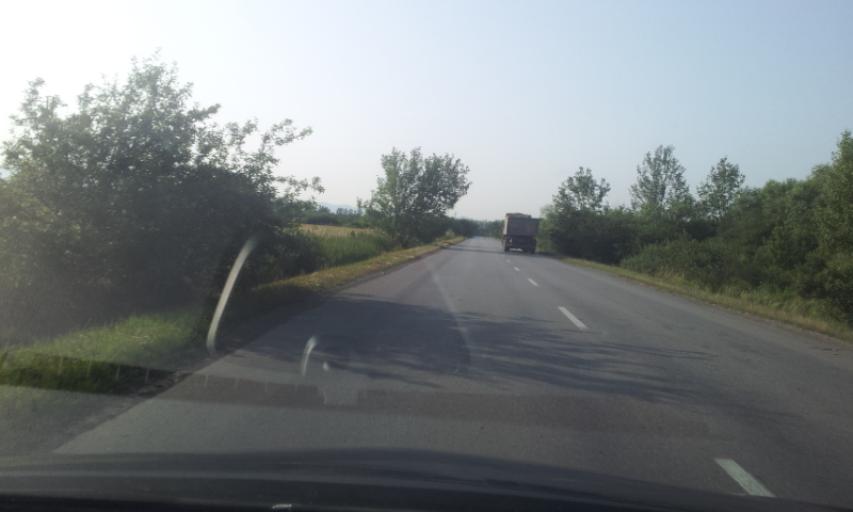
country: SK
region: Kosicky
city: Kosice
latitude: 48.6268
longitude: 21.2217
